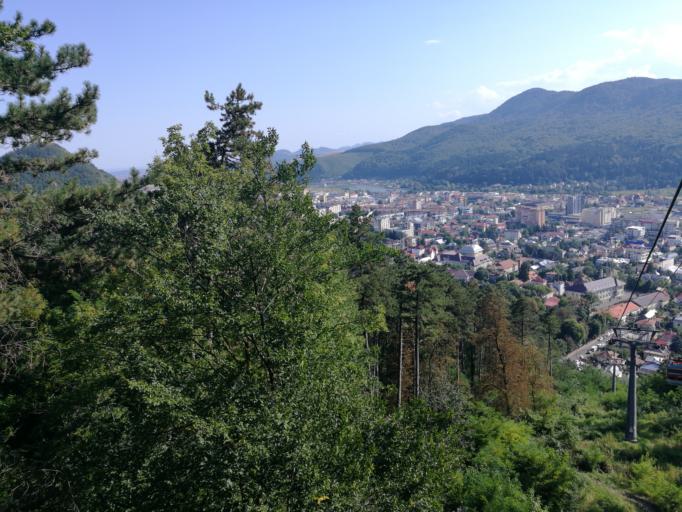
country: RO
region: Neamt
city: Piatra Neamt
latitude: 46.9396
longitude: 26.3654
